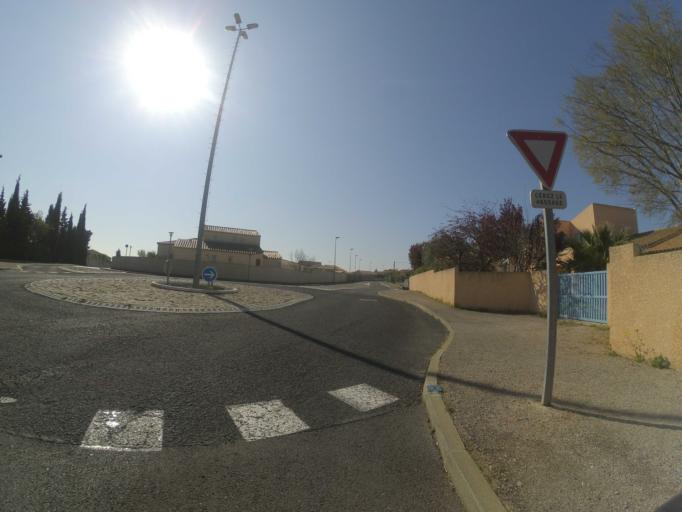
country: FR
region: Languedoc-Roussillon
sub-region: Departement des Pyrenees-Orientales
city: Thuir
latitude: 42.6226
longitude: 2.7511
